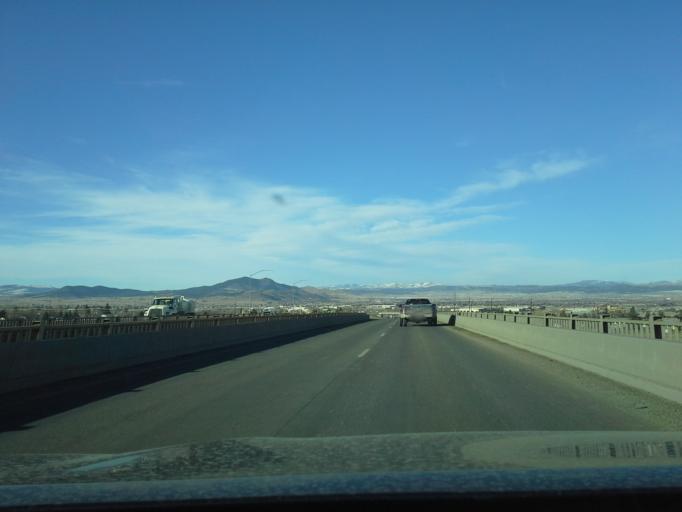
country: US
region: Montana
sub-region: Lewis and Clark County
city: Helena
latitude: 46.5985
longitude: -112.0030
